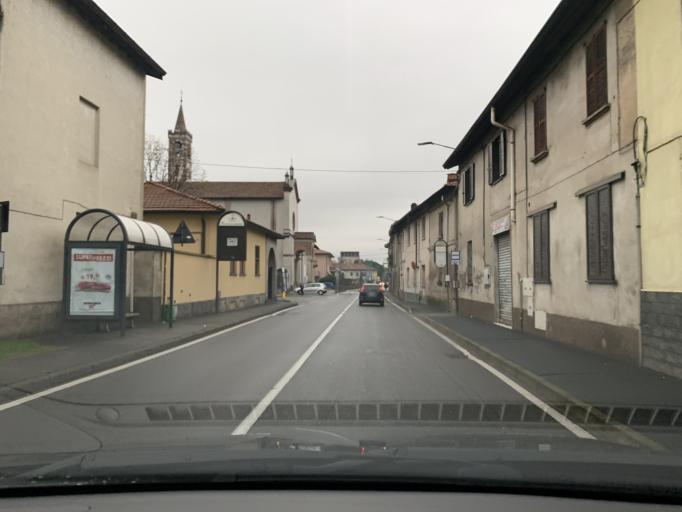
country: IT
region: Lombardy
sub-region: Provincia di Como
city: Rovello Porro
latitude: 45.6378
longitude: 9.0468
